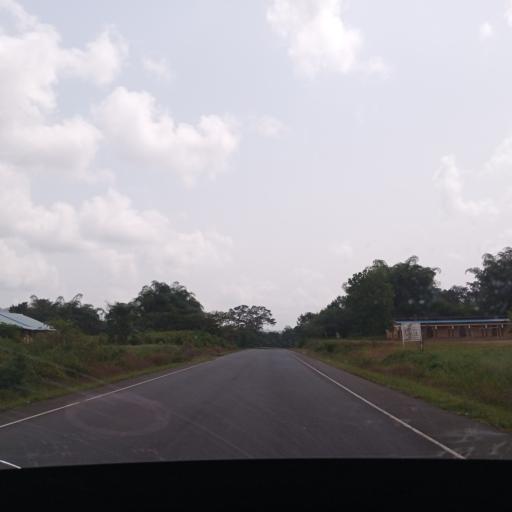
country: LR
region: Margibi
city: Kakata
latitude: 6.2430
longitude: -10.2886
